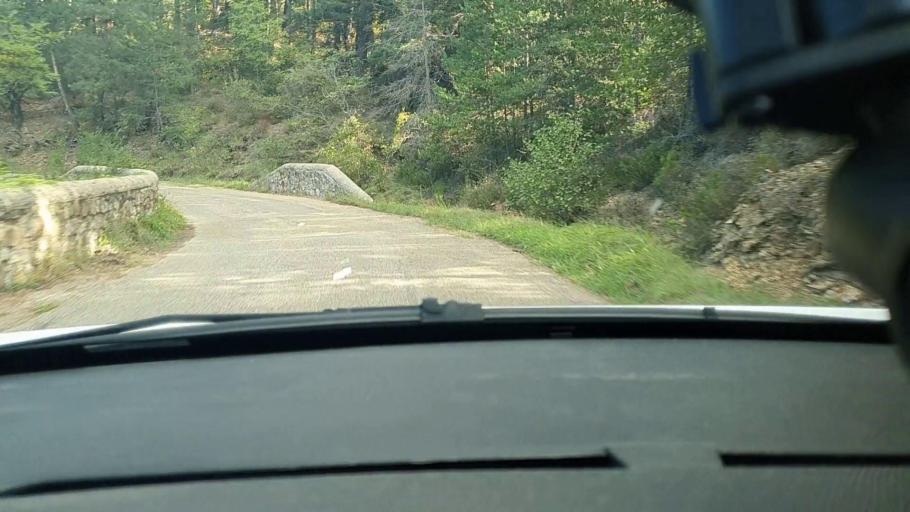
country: FR
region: Languedoc-Roussillon
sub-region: Departement du Gard
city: Besseges
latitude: 44.3816
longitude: 3.9919
